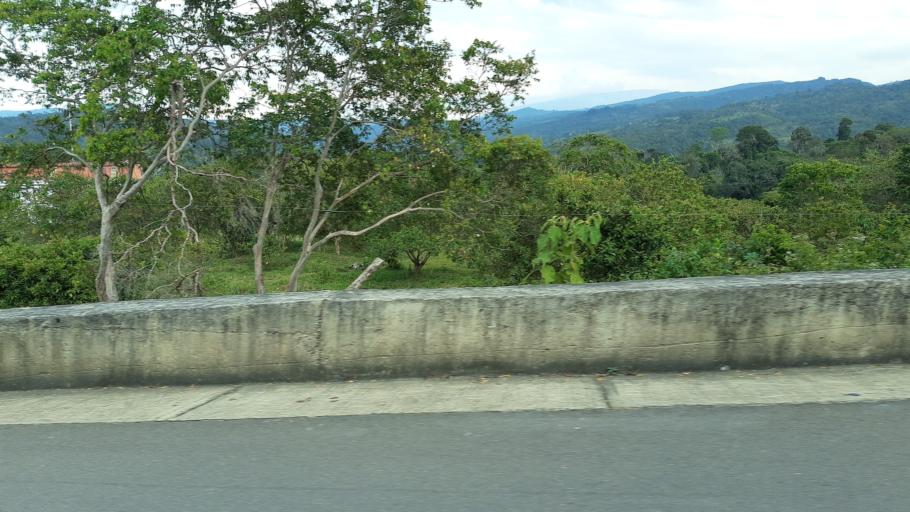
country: CO
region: Boyaca
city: Moniquira
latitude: 5.8331
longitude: -73.5919
